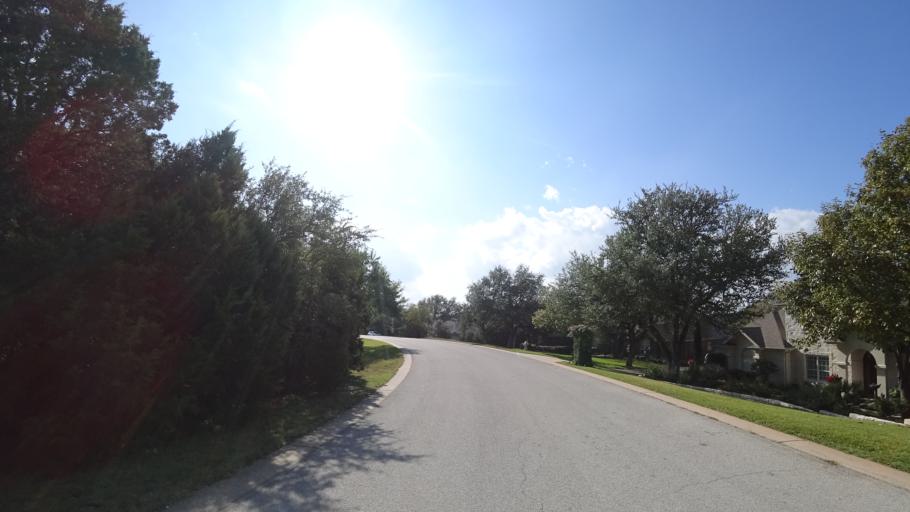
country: US
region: Texas
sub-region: Travis County
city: Lost Creek
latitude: 30.3072
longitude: -97.8587
